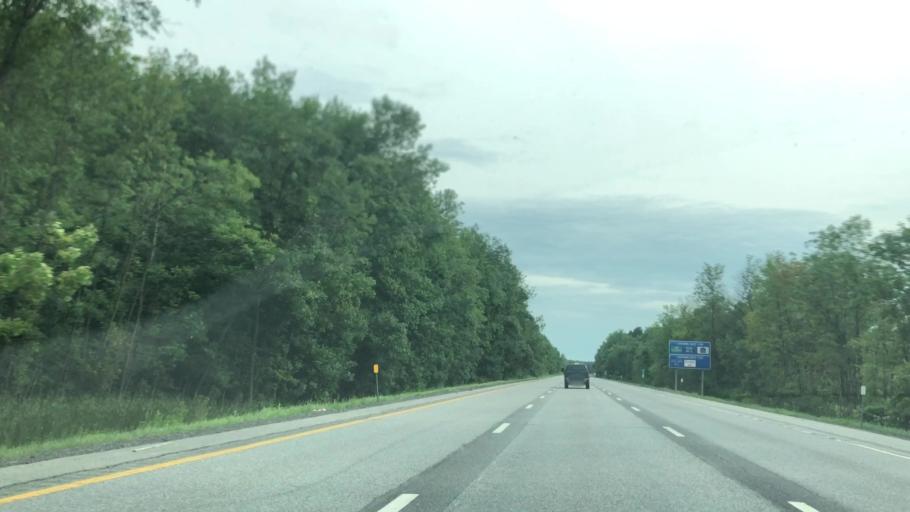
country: US
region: New York
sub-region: Saratoga County
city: Saratoga Springs
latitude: 43.0344
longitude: -73.7808
